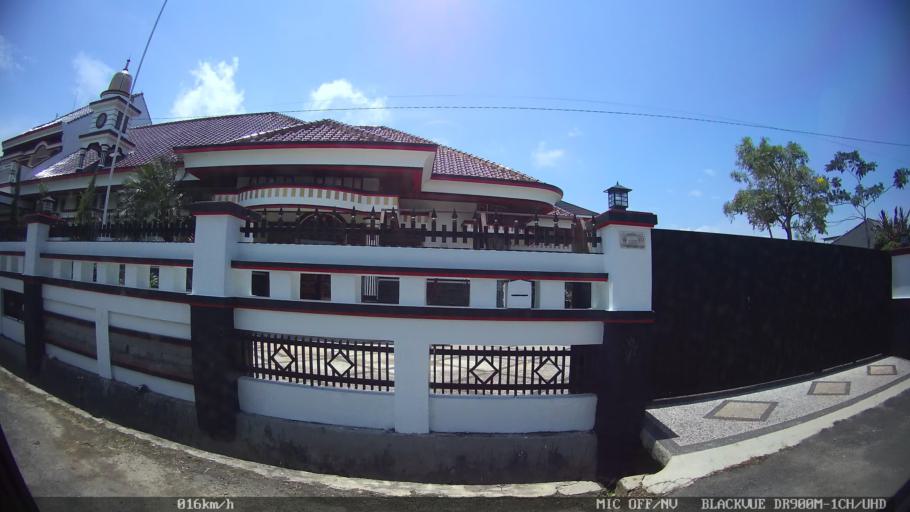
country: ID
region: Lampung
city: Kedaton
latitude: -5.3769
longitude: 105.2923
